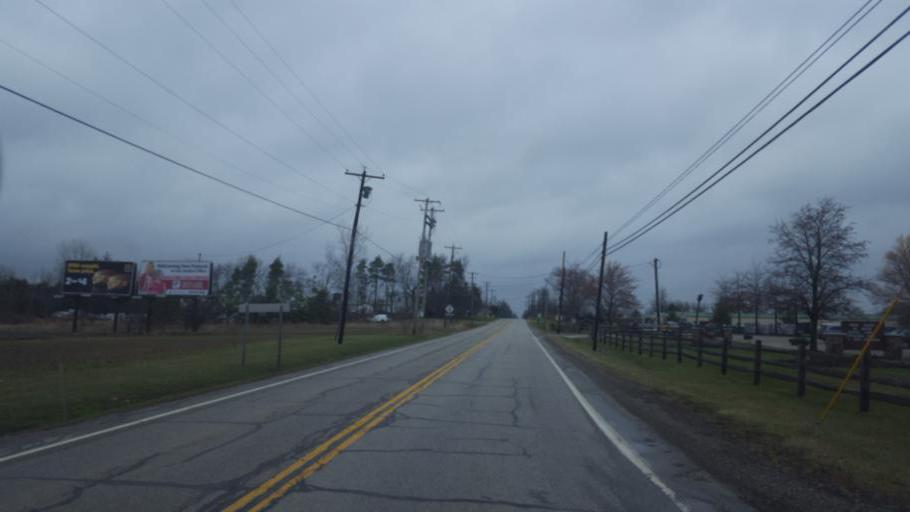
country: US
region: Ohio
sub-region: Medina County
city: Medina
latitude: 41.0781
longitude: -81.8643
